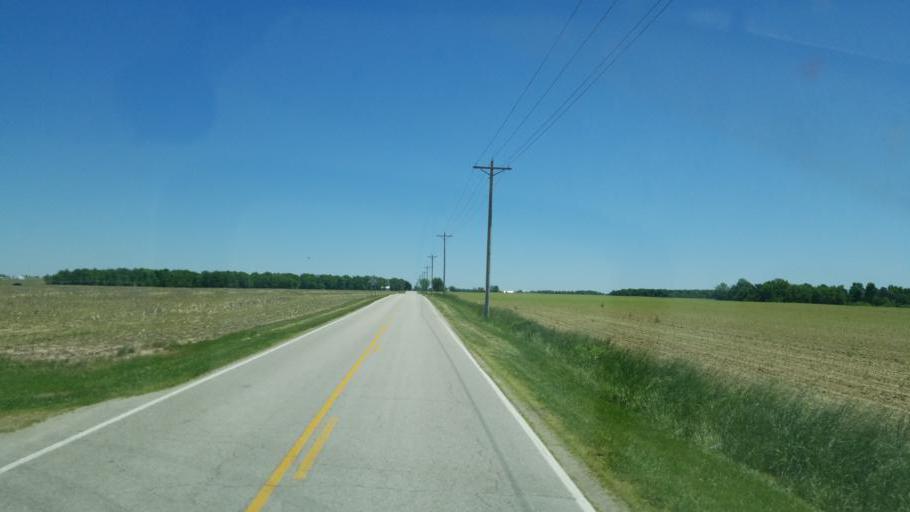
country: US
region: Ohio
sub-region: Darke County
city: Ansonia
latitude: 40.2649
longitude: -84.6995
